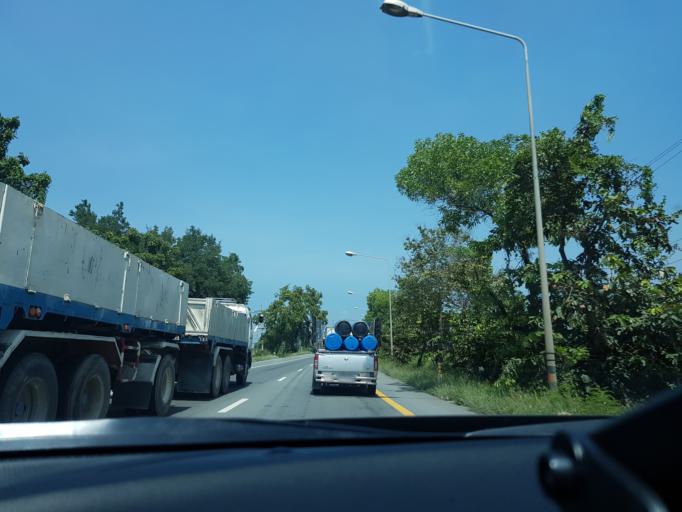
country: TH
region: Sara Buri
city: Saraburi
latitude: 14.5225
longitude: 100.8890
